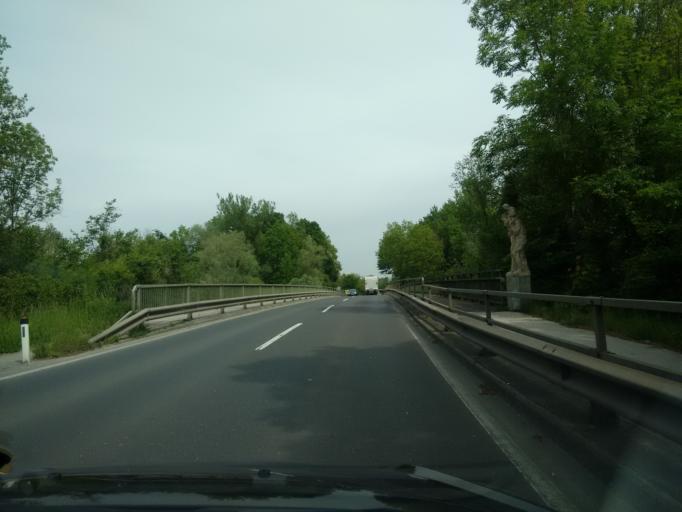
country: AT
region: Upper Austria
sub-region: Politischer Bezirk Linz-Land
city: Traun
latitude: 48.2133
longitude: 14.2412
